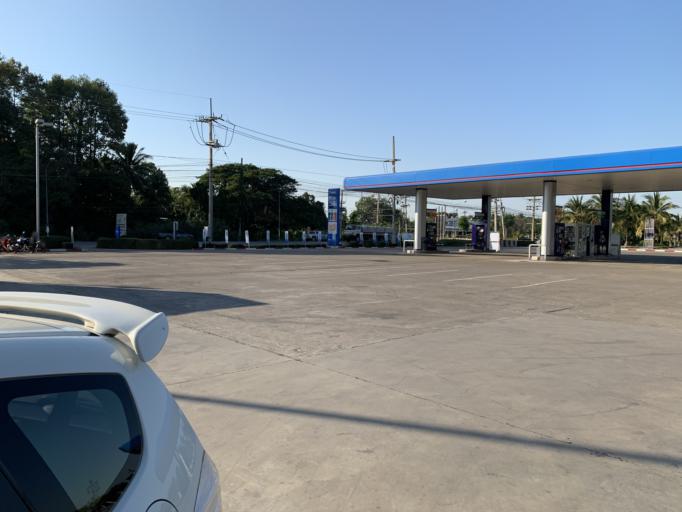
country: TH
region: Sukhothai
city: Sawankhalok
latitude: 17.3340
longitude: 99.8480
